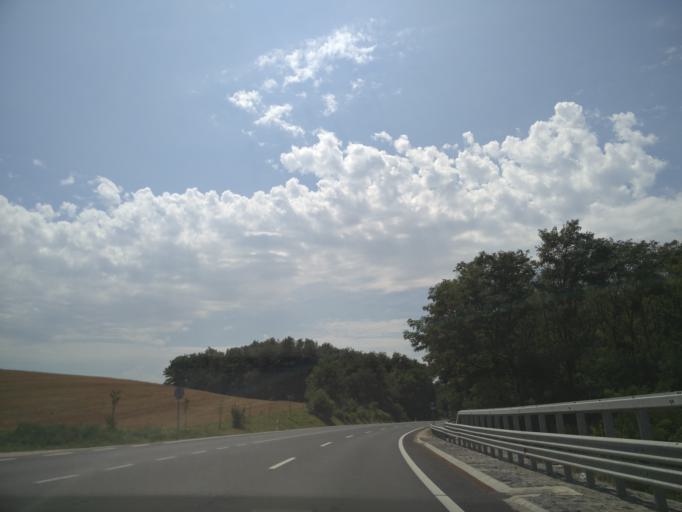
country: HU
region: Vas
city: Vasvar
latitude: 47.0677
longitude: 16.8367
